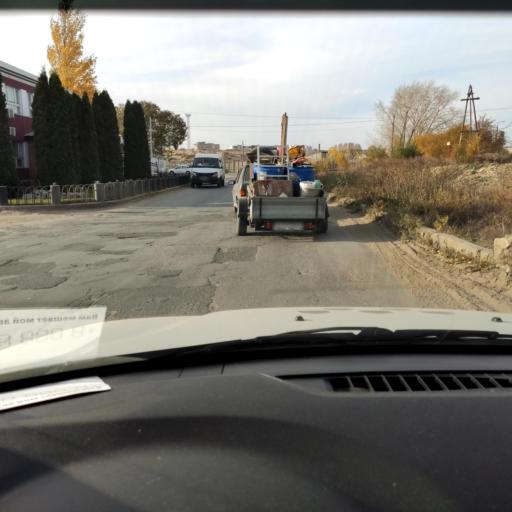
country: RU
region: Samara
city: Zhigulevsk
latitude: 53.4751
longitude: 49.4996
